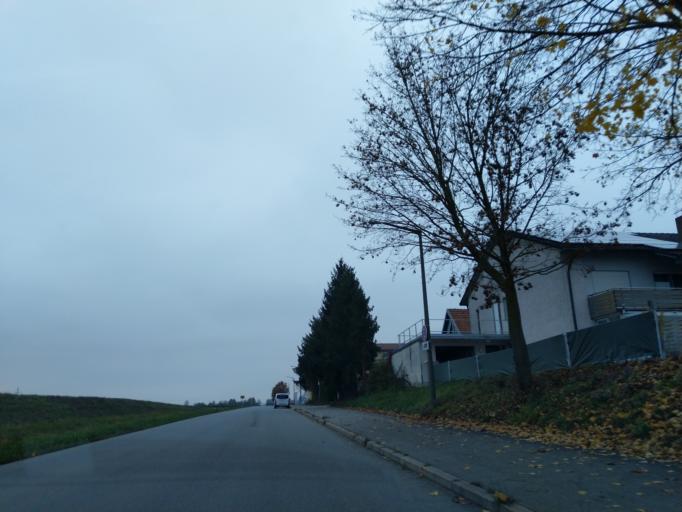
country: DE
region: Bavaria
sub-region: Lower Bavaria
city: Plattling
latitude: 48.7867
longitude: 12.8605
